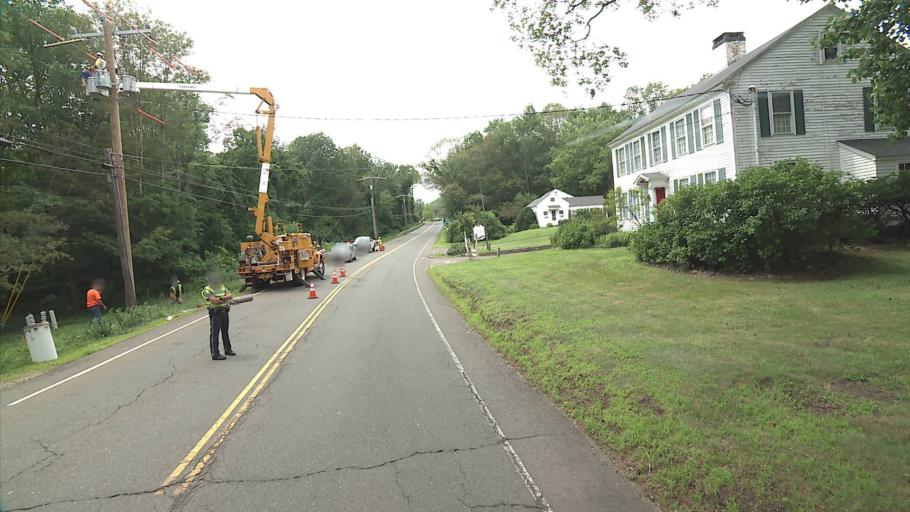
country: US
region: Connecticut
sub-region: Middlesex County
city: Clinton
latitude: 41.3572
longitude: -72.5612
